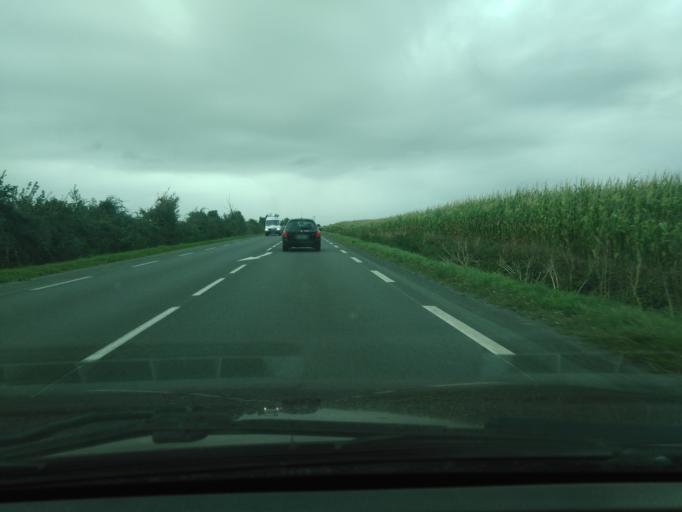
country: FR
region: Pays de la Loire
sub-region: Departement de la Vendee
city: Sainte-Gemme-la-Plaine
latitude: 46.4543
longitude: -1.1047
